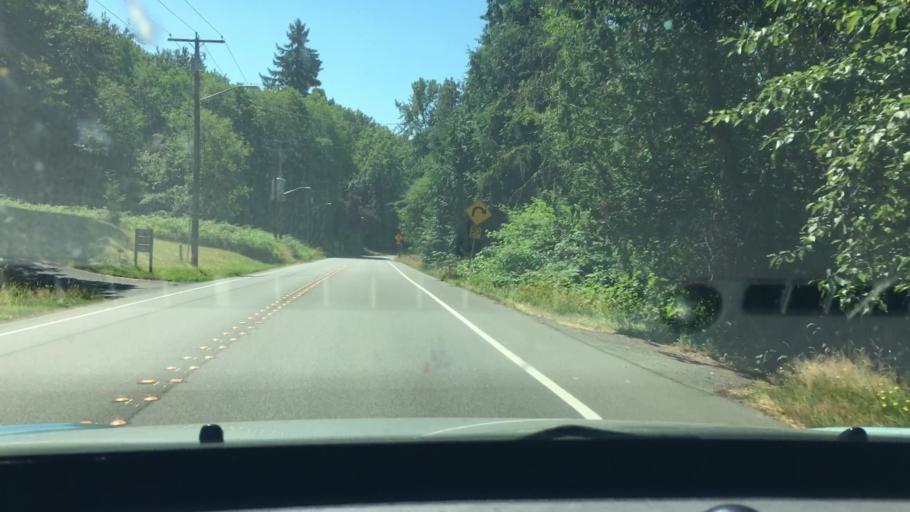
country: US
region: Washington
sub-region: King County
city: Newcastle
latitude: 47.5374
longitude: -122.1291
